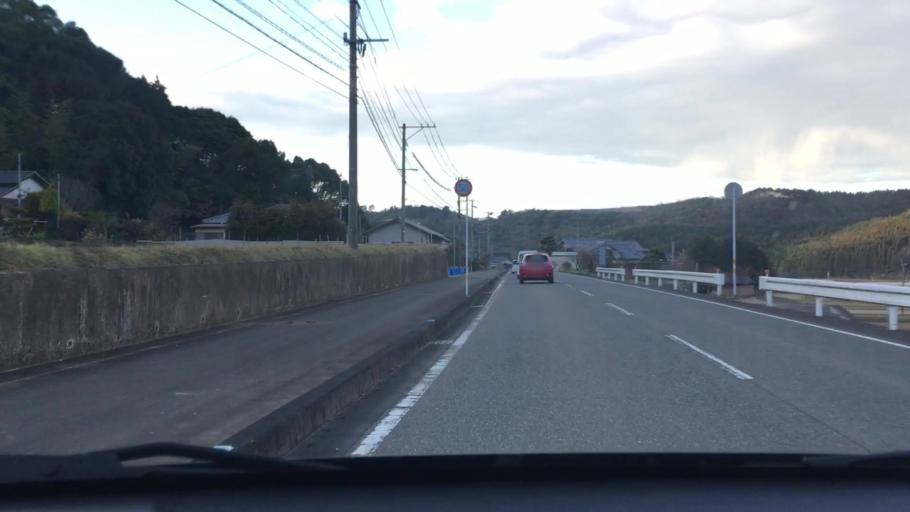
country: JP
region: Oita
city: Bungo-Takada-shi
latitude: 33.4981
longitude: 131.3765
